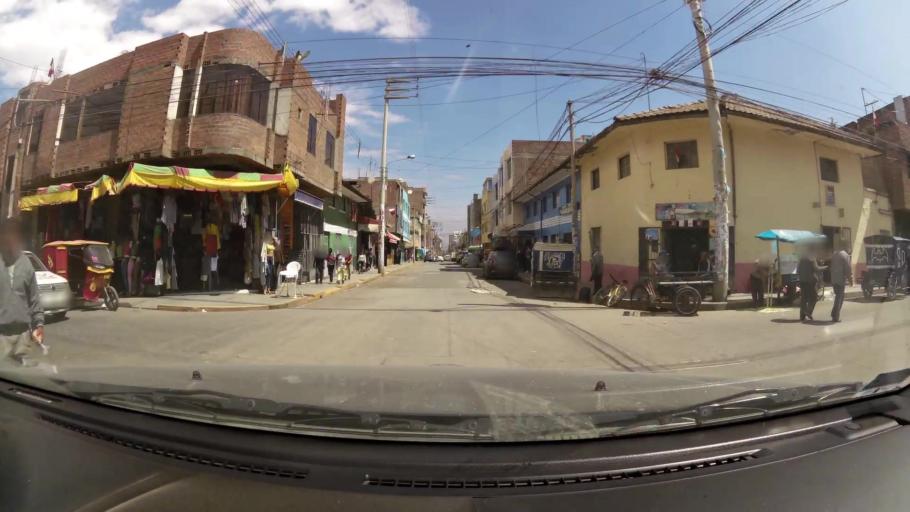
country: PE
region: Junin
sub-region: Provincia de Huancayo
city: Huancayo
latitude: -12.0703
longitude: -75.2016
